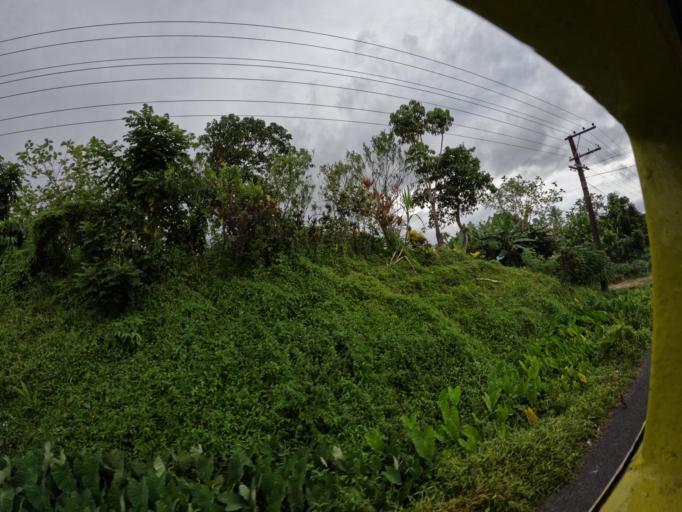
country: FJ
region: Central
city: Suva
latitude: -18.0757
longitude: 178.4599
